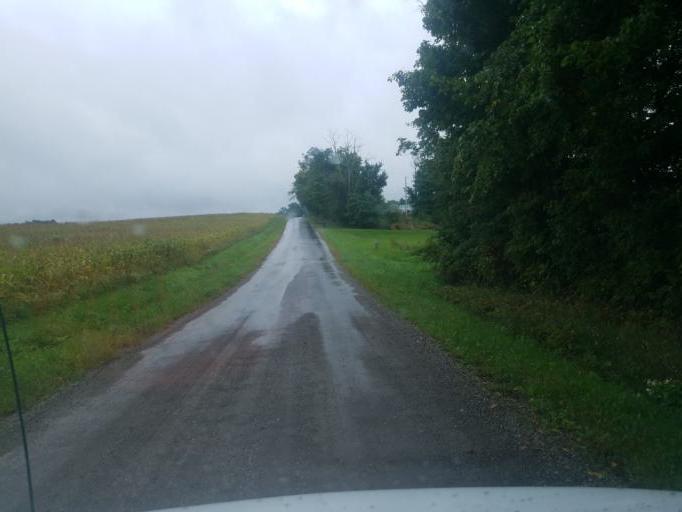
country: US
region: Ohio
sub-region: Wayne County
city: West Salem
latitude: 40.9300
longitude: -82.0871
